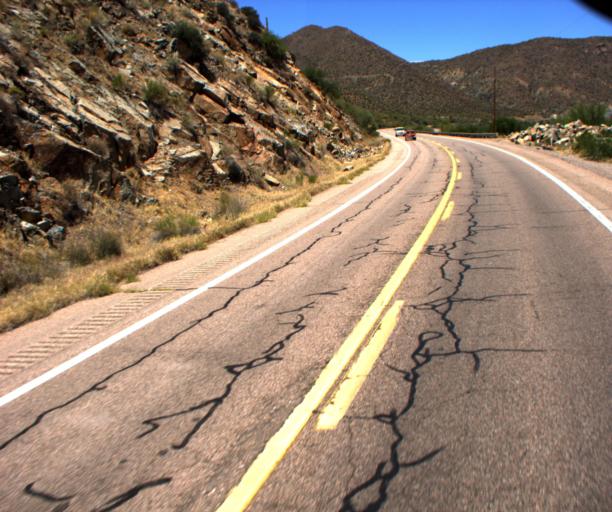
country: US
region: Arizona
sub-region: Pinal County
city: Kearny
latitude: 33.0573
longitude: -110.7197
